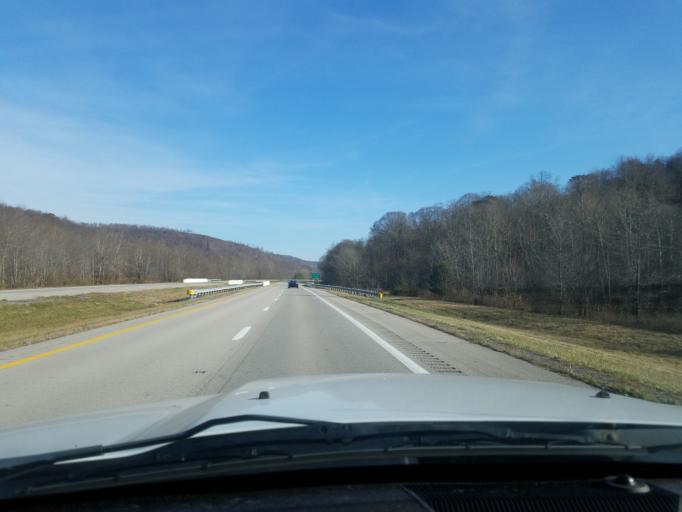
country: US
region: Ohio
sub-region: Adams County
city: Peebles
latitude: 39.0385
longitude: -83.2419
